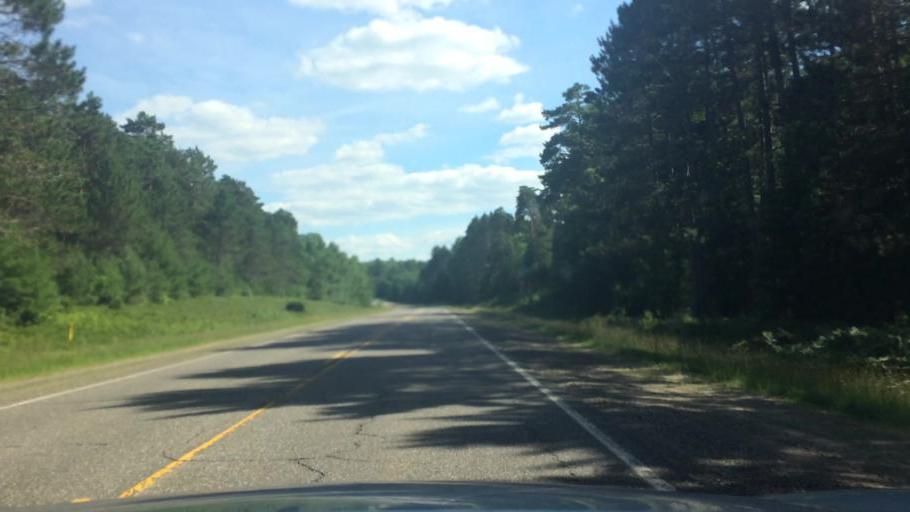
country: US
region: Wisconsin
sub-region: Vilas County
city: Lac du Flambeau
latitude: 46.0498
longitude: -89.6500
